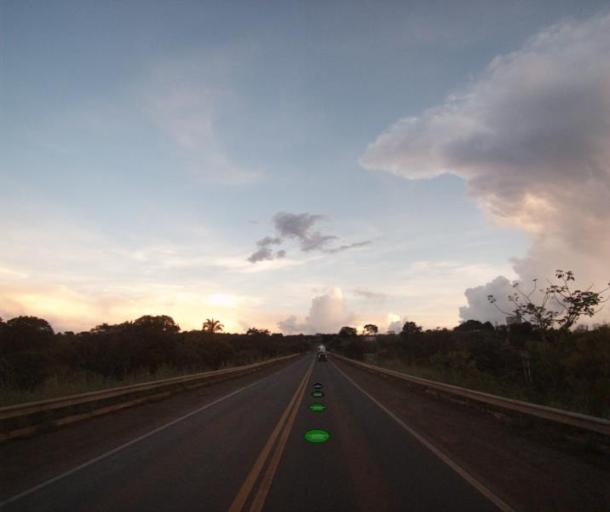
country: BR
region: Goias
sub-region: Uruacu
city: Uruacu
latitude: -14.5021
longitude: -49.1497
